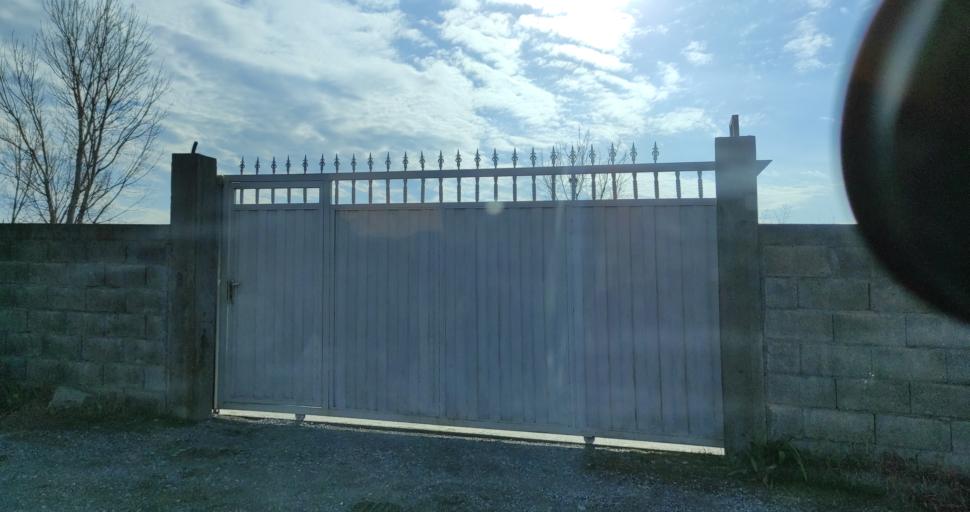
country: AL
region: Lezhe
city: Lezhe
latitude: 41.7779
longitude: 19.6336
